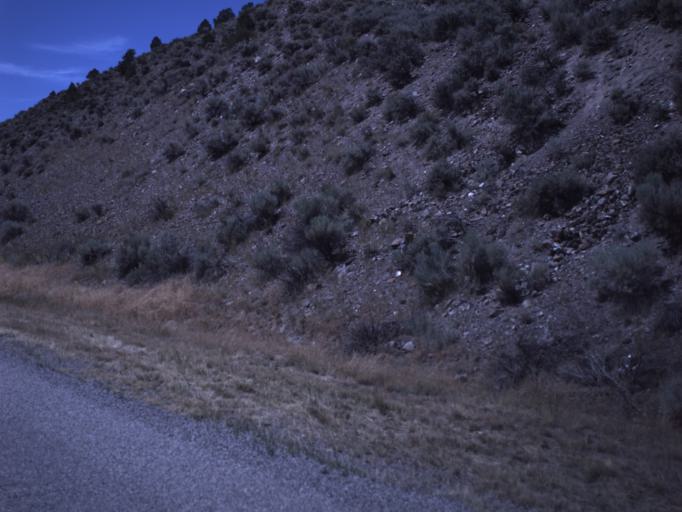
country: US
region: Utah
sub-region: Piute County
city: Junction
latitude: 38.0788
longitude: -112.3400
